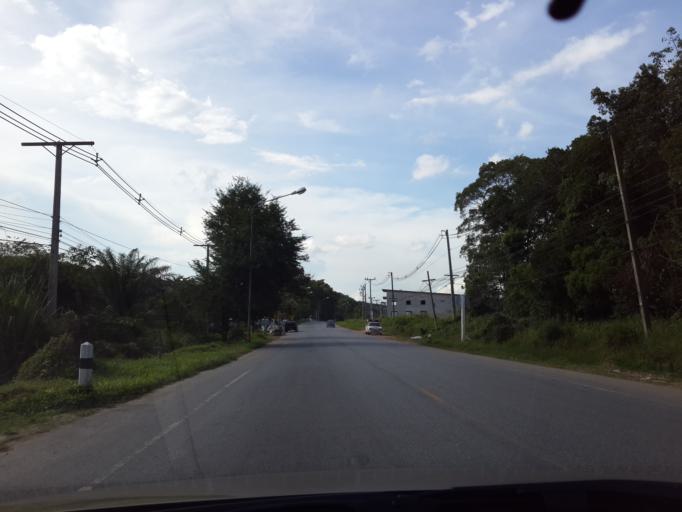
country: TH
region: Yala
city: Krong Pi Nang
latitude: 6.4598
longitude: 101.3313
